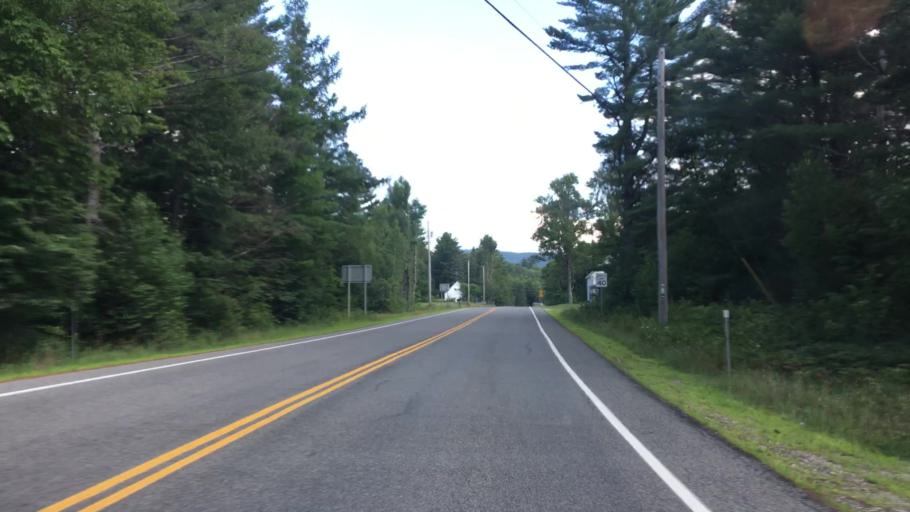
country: US
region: New Hampshire
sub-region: Grafton County
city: Woodstock
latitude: 44.0953
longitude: -71.8309
